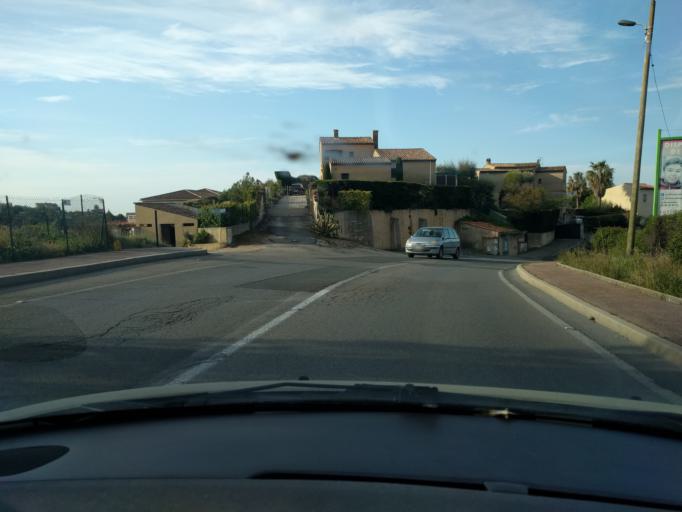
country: FR
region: Provence-Alpes-Cote d'Azur
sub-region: Departement des Alpes-Maritimes
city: Cannes
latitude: 43.5625
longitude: 6.9774
